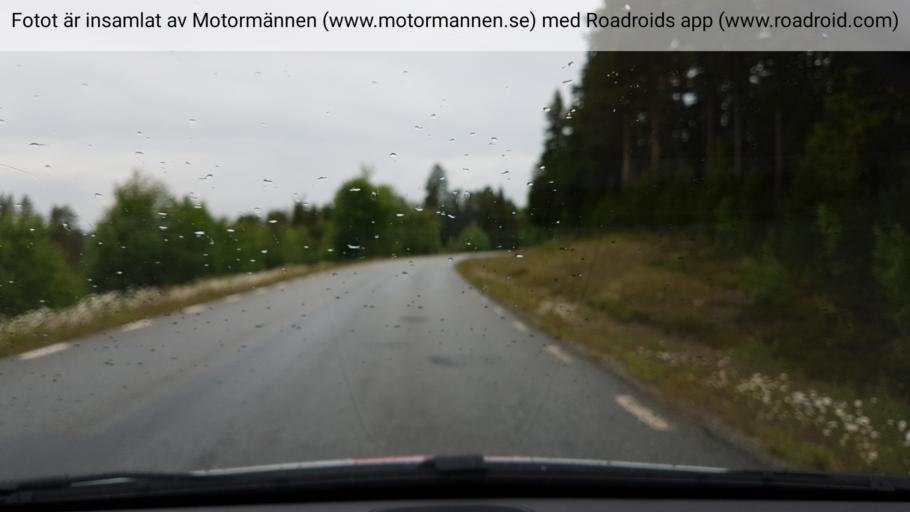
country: SE
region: Vaesterbotten
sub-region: Dorotea Kommun
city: Dorotea
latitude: 64.1395
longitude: 16.0713
